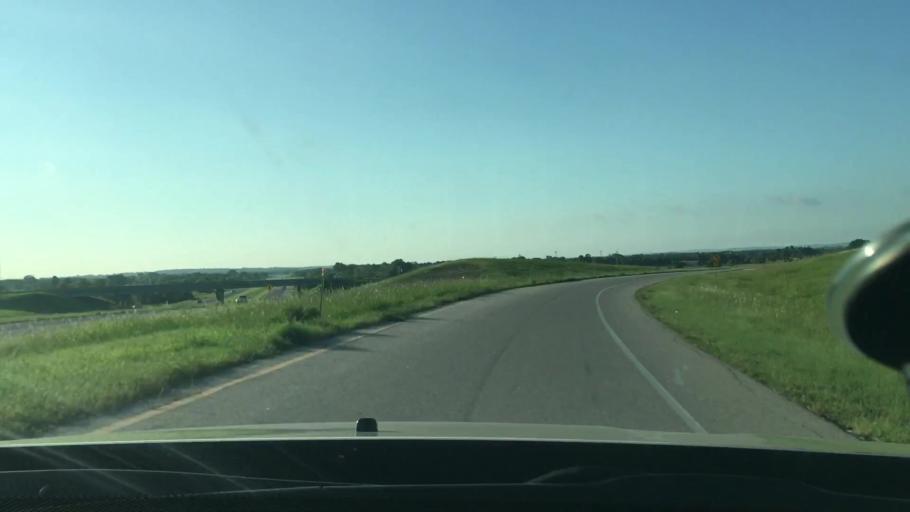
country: US
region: Oklahoma
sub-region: Pontotoc County
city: Ada
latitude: 34.7283
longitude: -96.6376
